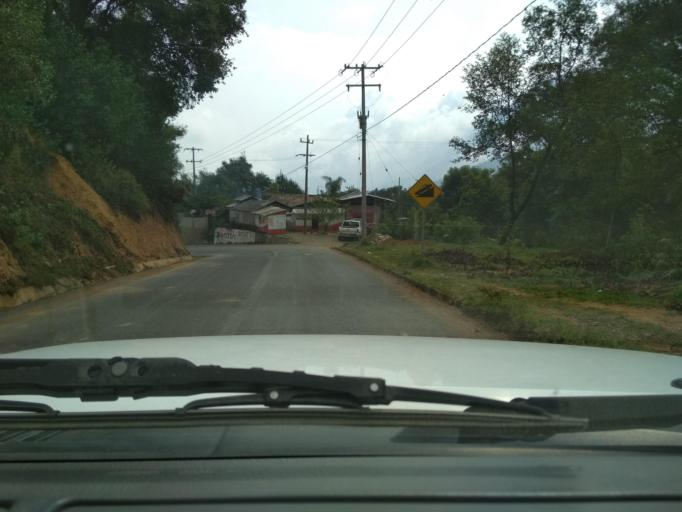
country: MX
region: Veracruz
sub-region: Camerino Z. Mendoza
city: Necoxtla
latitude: 18.7577
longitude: -97.1531
